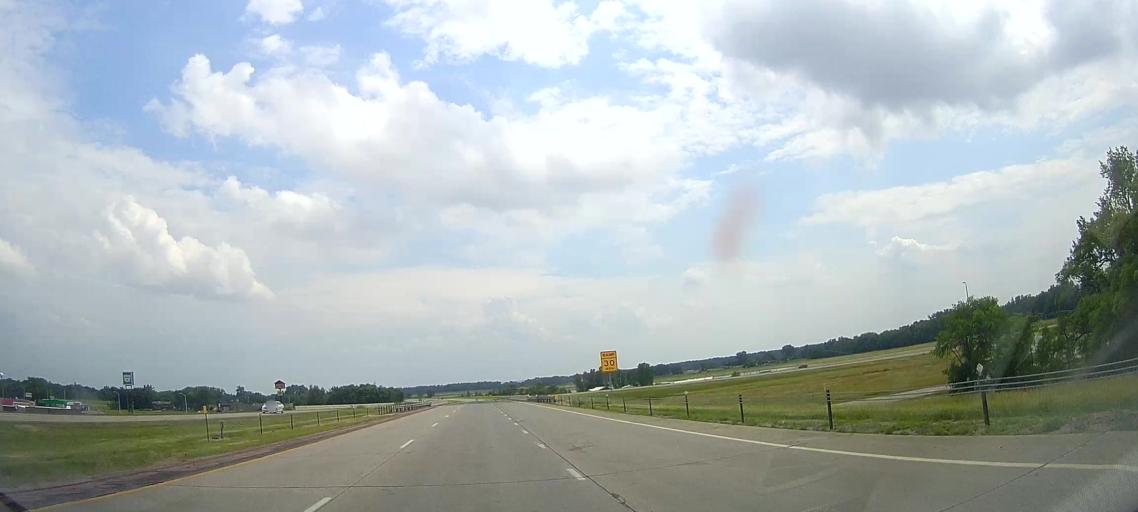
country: US
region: South Dakota
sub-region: Union County
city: Elk Point
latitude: 42.6928
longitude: -96.6974
